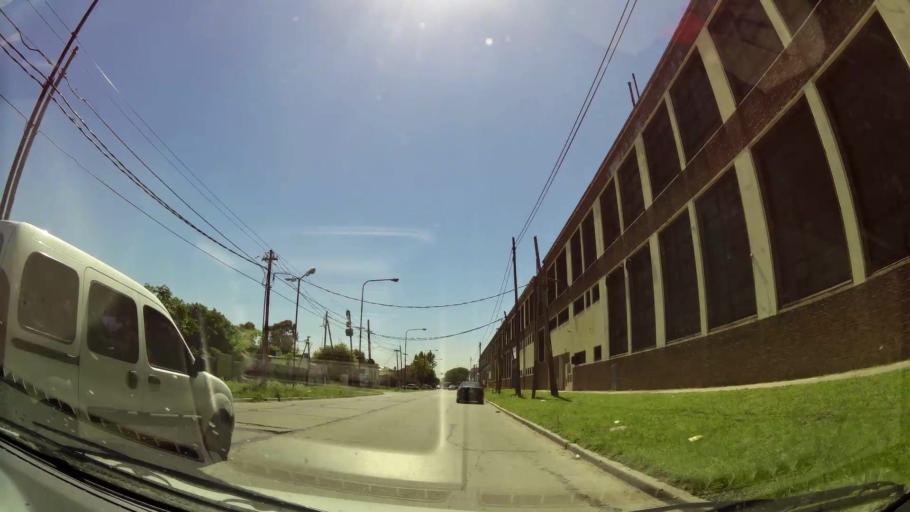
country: AR
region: Buenos Aires
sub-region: Partido de Quilmes
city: Quilmes
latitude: -34.7216
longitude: -58.2849
